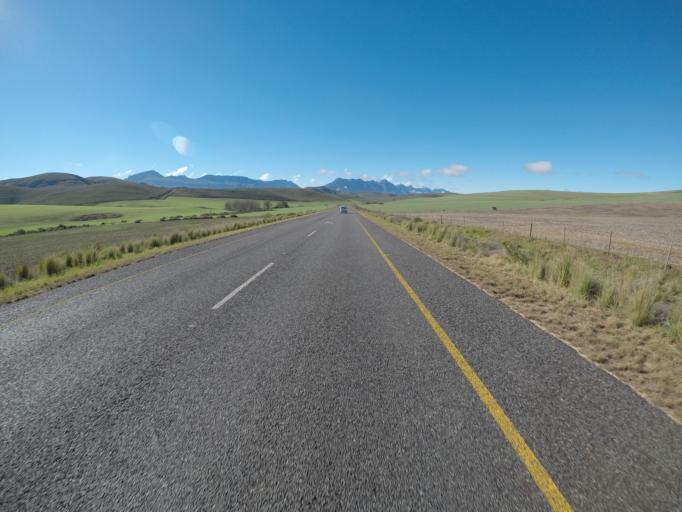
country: ZA
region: Western Cape
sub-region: Overberg District Municipality
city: Caledon
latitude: -34.0977
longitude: 19.5333
